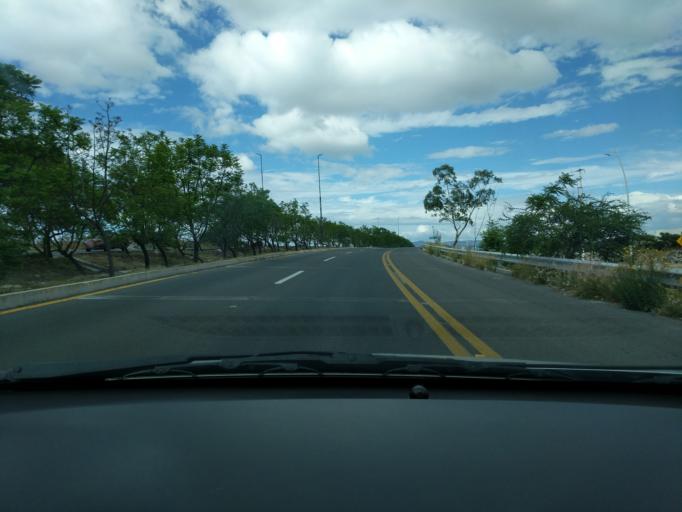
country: MX
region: Queretaro
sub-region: El Marques
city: La Pradera
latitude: 20.6641
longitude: -100.3171
